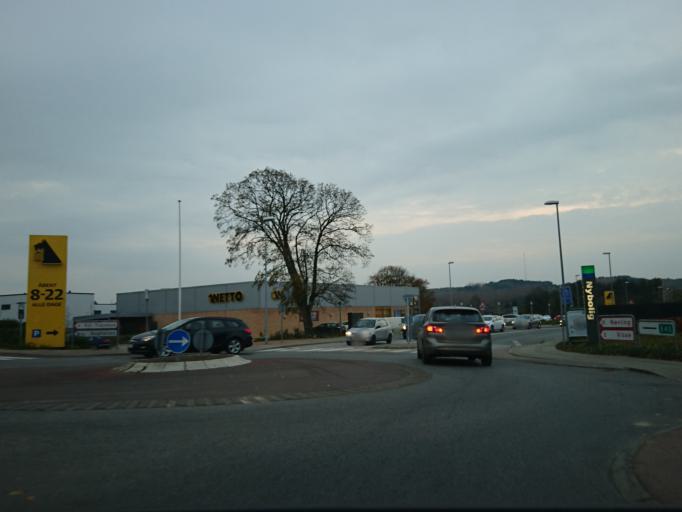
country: DK
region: North Denmark
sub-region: Alborg Kommune
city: Aalborg
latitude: 57.0072
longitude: 9.9267
